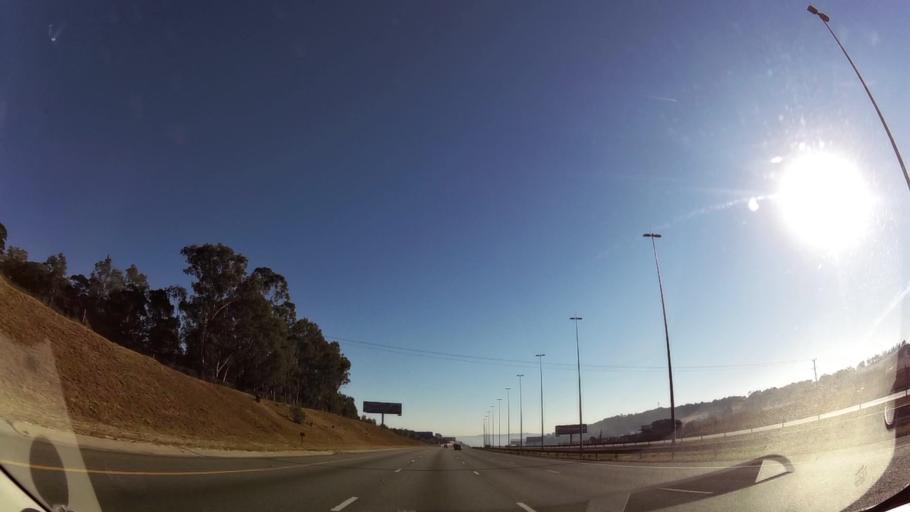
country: ZA
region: Gauteng
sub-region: City of Tshwane Metropolitan Municipality
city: Centurion
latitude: -25.9015
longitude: 28.2549
